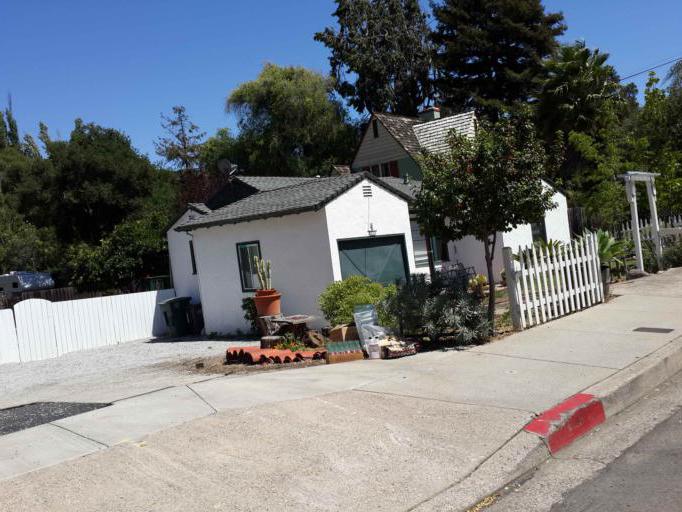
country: US
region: California
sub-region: San Luis Obispo County
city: San Luis Obispo
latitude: 35.2903
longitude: -120.6717
